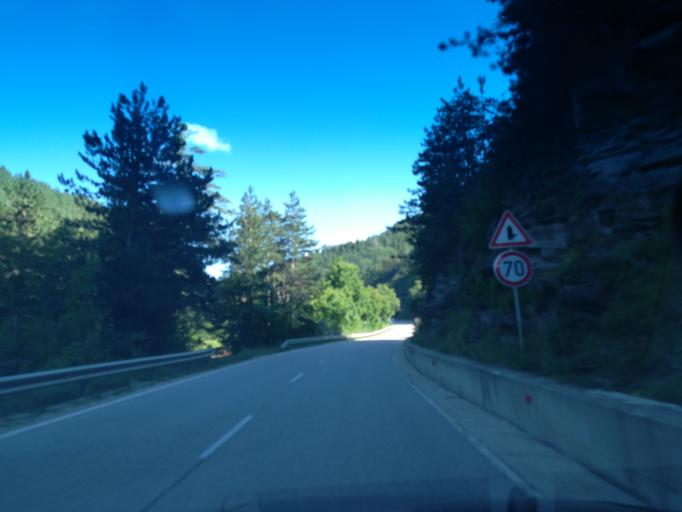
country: BG
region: Smolyan
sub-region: Obshtina Chepelare
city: Chepelare
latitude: 41.8306
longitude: 24.6854
